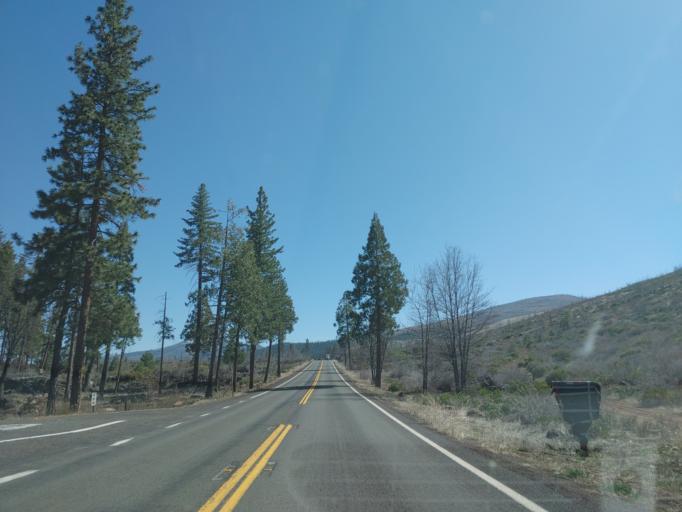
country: US
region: California
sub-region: Shasta County
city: Burney
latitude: 40.7791
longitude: -121.5036
